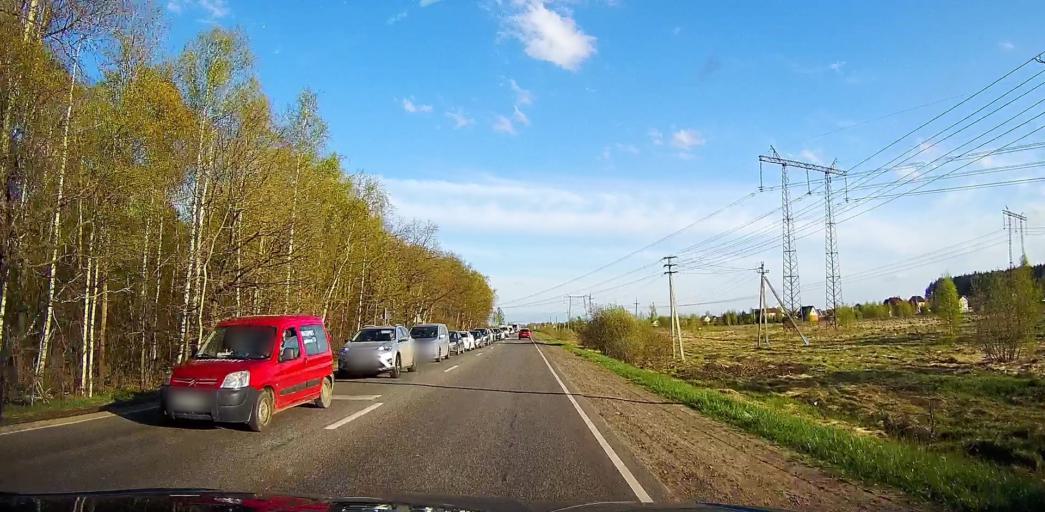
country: RU
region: Moskovskaya
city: Bronnitsy
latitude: 55.3767
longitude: 38.2111
